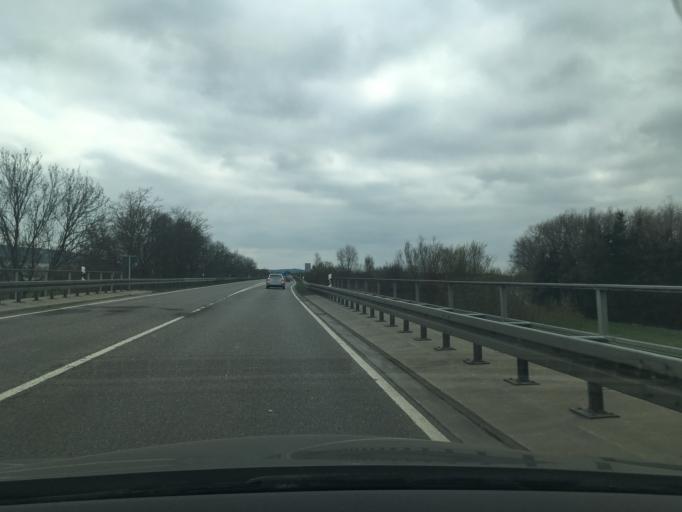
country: DE
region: Baden-Wuerttemberg
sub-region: Tuebingen Region
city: Hochdorf
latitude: 48.0360
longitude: 9.7863
